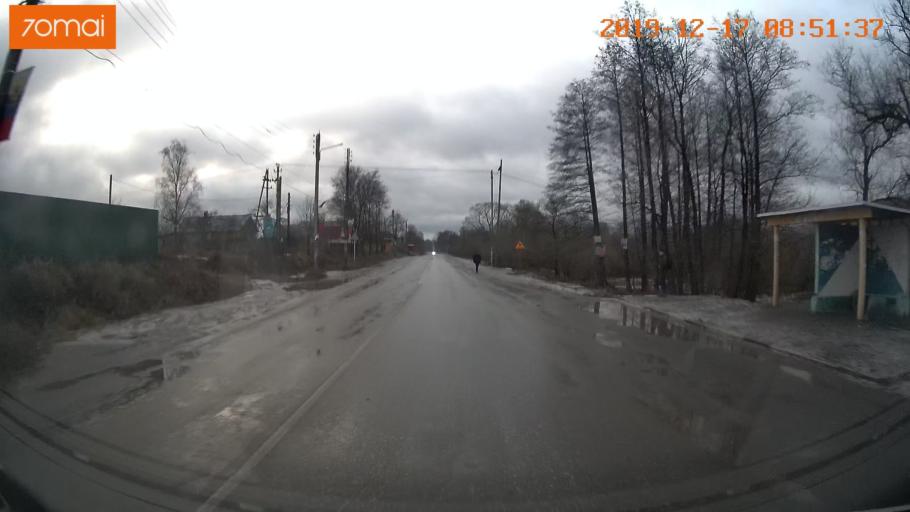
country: RU
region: Vladimir
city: Kosterevo
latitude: 55.9566
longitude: 39.6328
